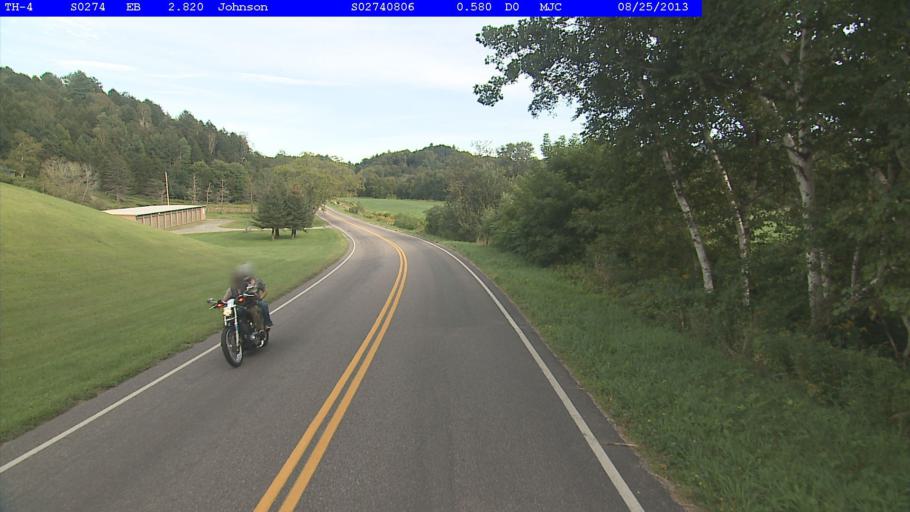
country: US
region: Vermont
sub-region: Lamoille County
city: Johnson
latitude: 44.6535
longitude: -72.7403
